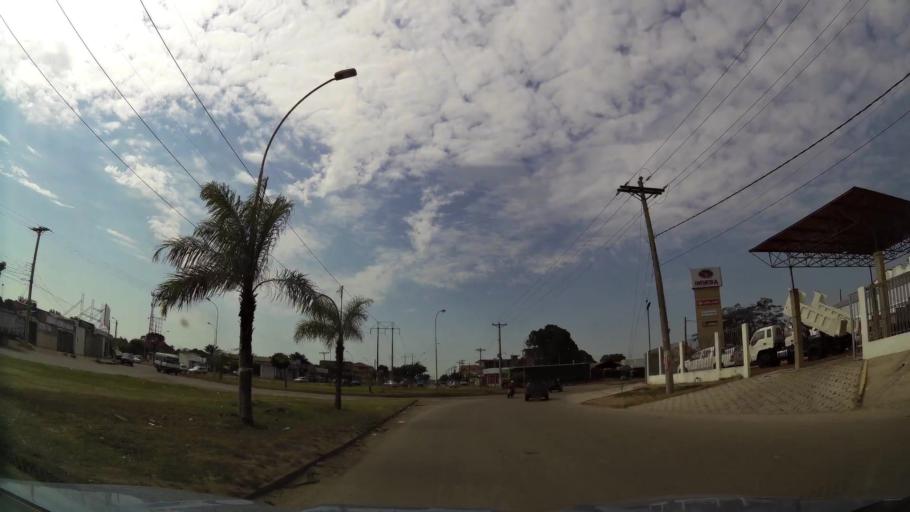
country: BO
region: Santa Cruz
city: Santa Cruz de la Sierra
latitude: -17.7444
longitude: -63.1614
